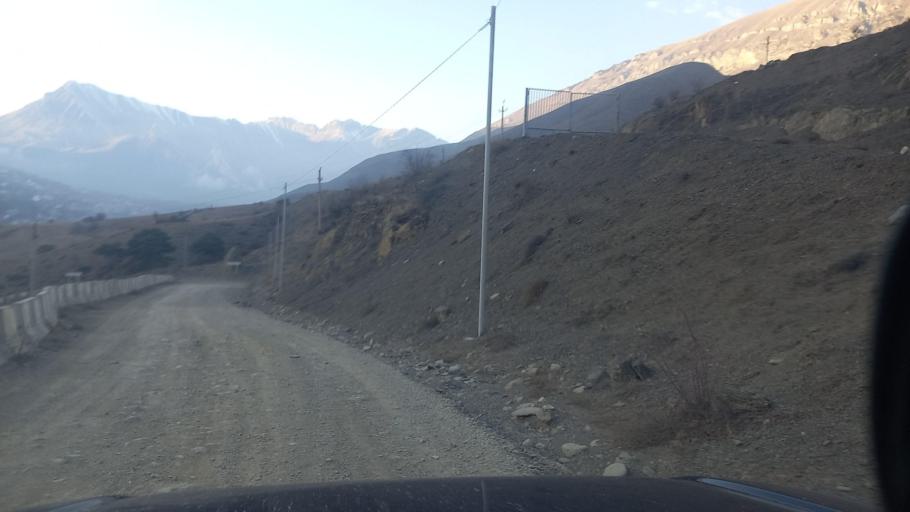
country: RU
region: Ingushetiya
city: Dzhayrakh
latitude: 42.8178
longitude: 44.7031
